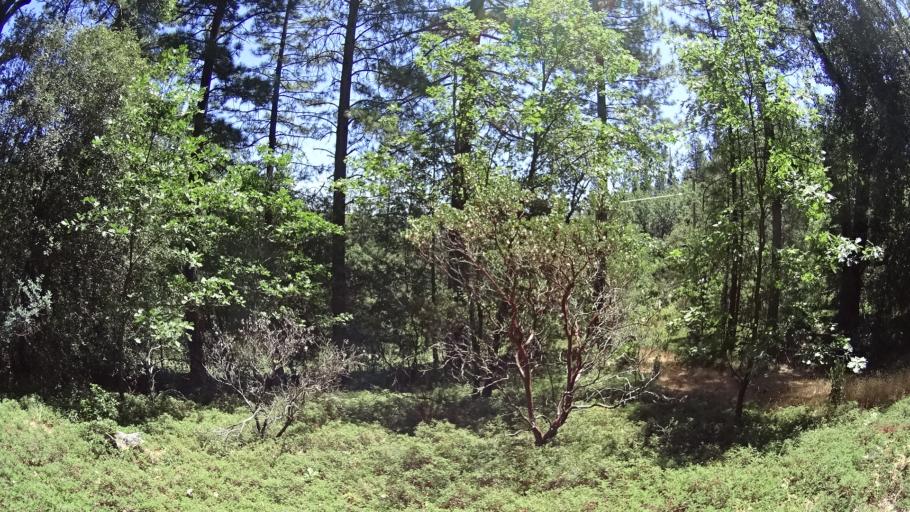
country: US
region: California
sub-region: Calaveras County
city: Forest Meadows
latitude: 38.1579
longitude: -120.3974
